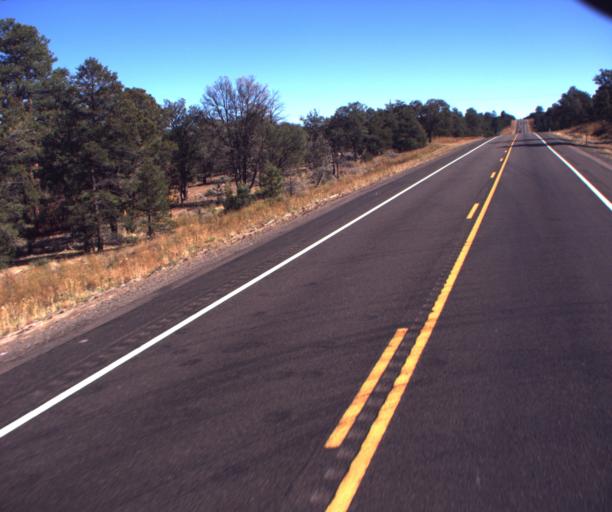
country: US
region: Arizona
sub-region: Apache County
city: Ganado
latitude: 35.7094
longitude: -109.3215
